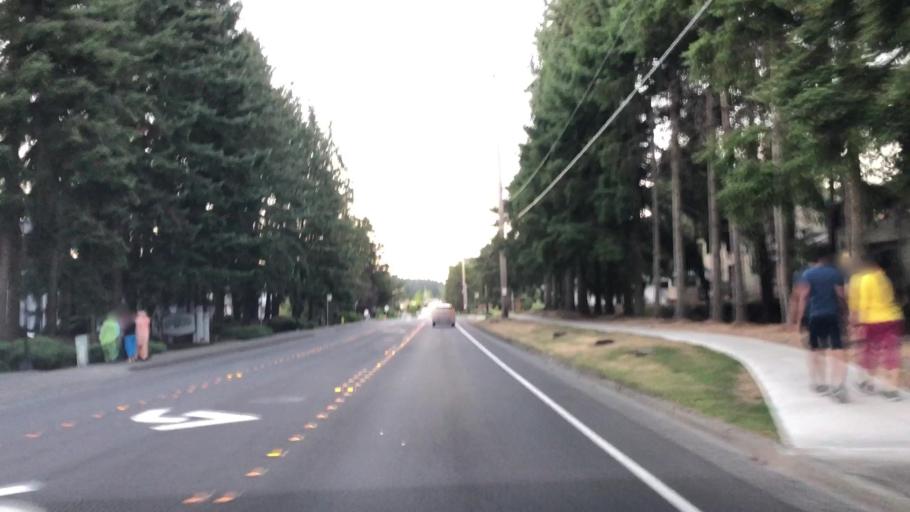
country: US
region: Washington
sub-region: King County
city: Bellevue
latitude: 47.6216
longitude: -122.1537
